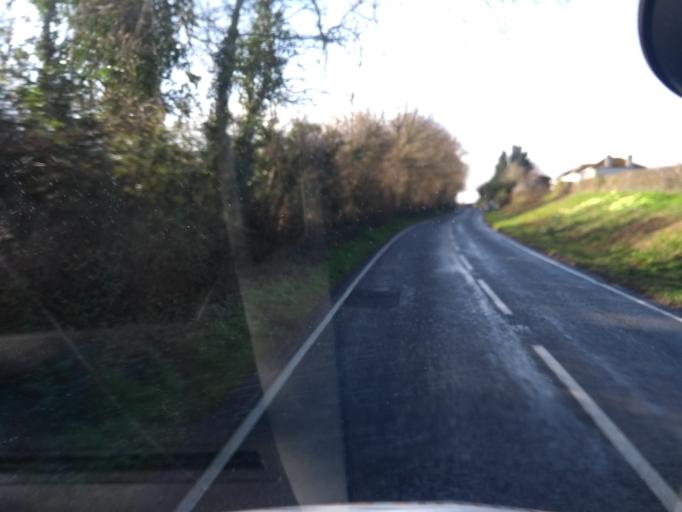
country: GB
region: England
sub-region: Somerset
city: Yeovil
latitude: 50.9625
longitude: -2.6199
